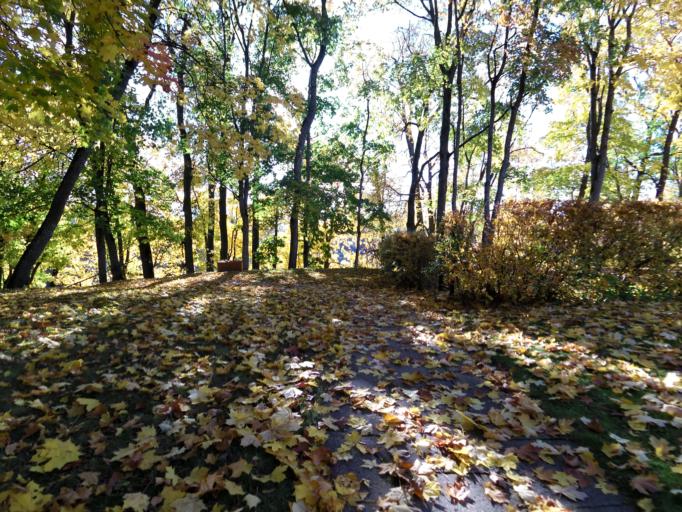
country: LT
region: Vilnius County
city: Justiniskes
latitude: 54.7202
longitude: 25.1973
